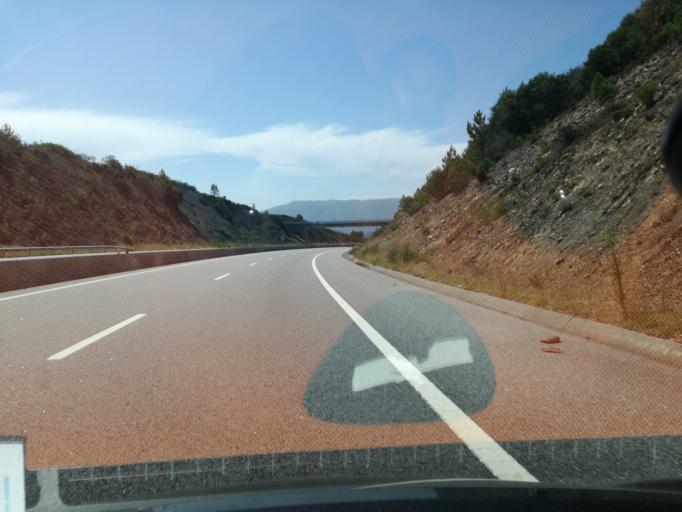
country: PT
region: Viana do Castelo
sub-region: Caminha
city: Vila Praia de Ancora
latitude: 41.8309
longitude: -8.7869
